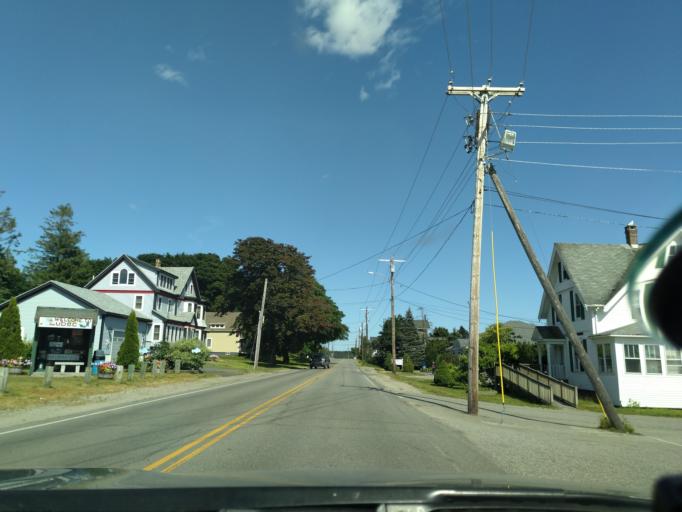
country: US
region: Maine
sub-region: Washington County
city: Eastport
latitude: 44.8578
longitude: -66.9900
